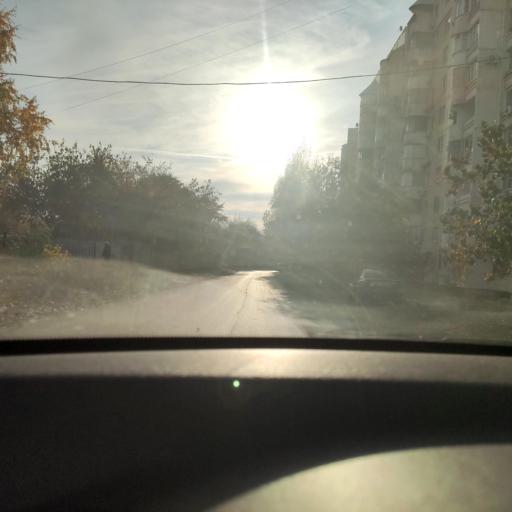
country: RU
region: Samara
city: Samara
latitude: 53.1875
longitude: 50.1444
